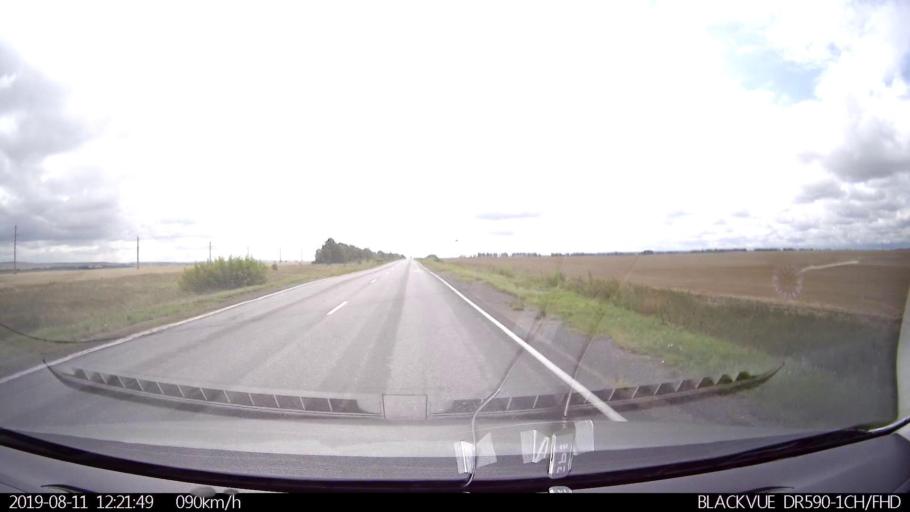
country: RU
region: Ulyanovsk
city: Ignatovka
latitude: 53.9163
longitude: 47.9563
